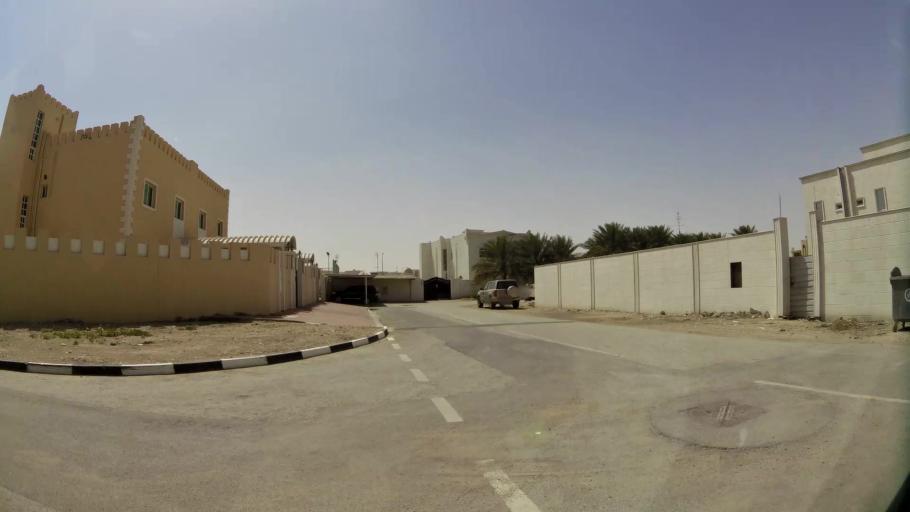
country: QA
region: Baladiyat Umm Salal
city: Umm Salal Muhammad
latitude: 25.3698
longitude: 51.4314
